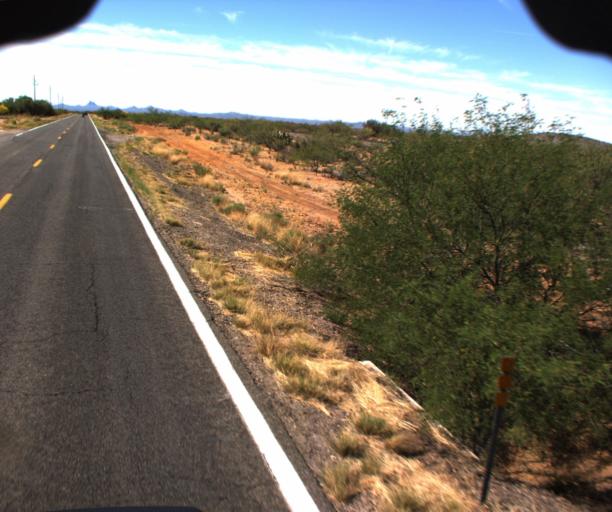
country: US
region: Arizona
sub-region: Yavapai County
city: Congress
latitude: 34.1405
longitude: -112.8414
